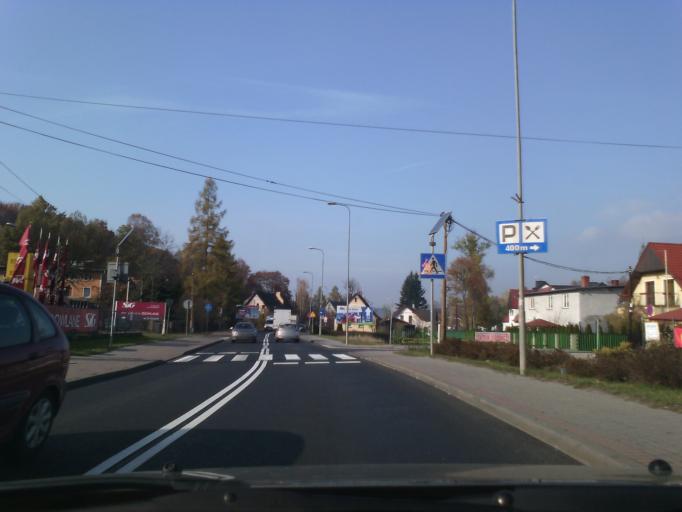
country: PL
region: Lower Silesian Voivodeship
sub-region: Powiat jeleniogorski
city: Myslakowice
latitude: 50.9090
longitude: 15.8330
